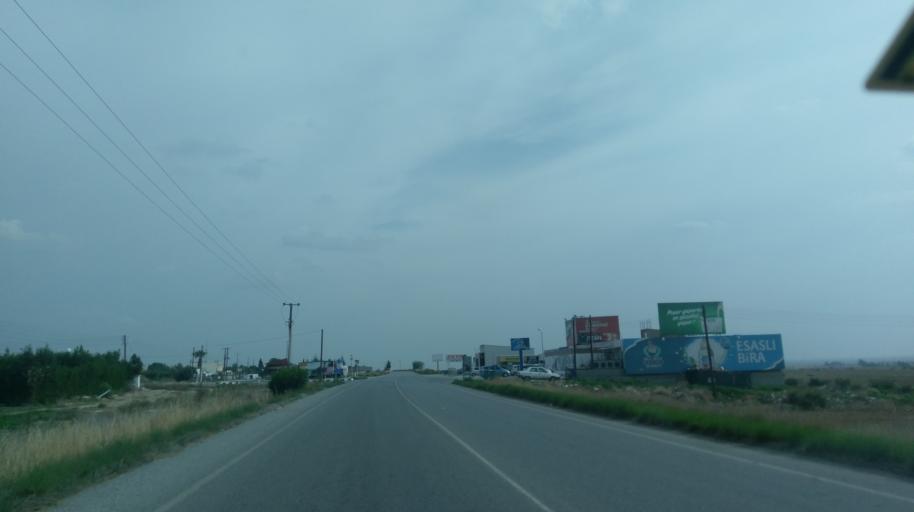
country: CY
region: Ammochostos
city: Lefkonoiko
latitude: 35.2423
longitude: 33.5971
